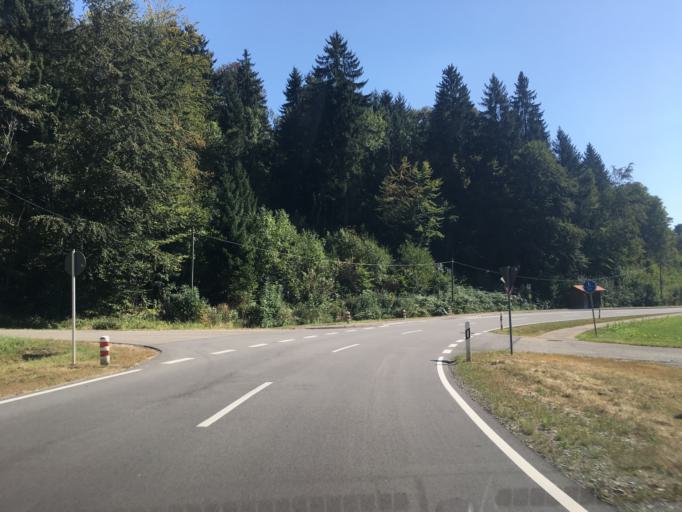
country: DE
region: Baden-Wuerttemberg
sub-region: Tuebingen Region
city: Munsingen
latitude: 48.3833
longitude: 9.4866
